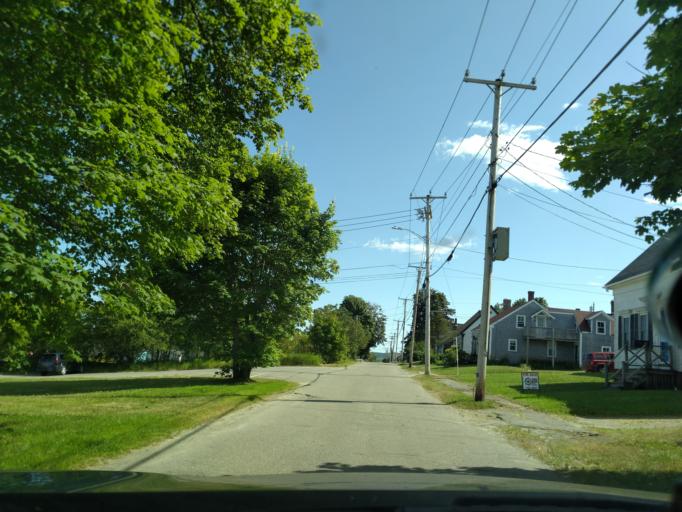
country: US
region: Maine
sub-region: Washington County
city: Eastport
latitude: 44.8604
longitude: -66.9842
